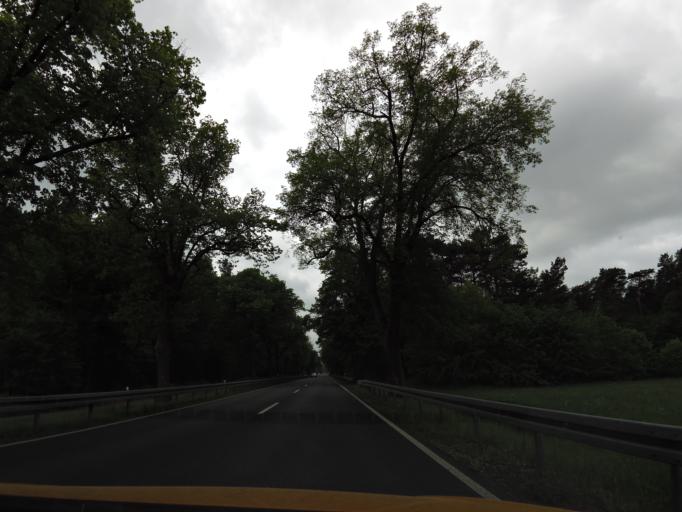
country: DE
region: Brandenburg
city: Beelitz
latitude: 52.1925
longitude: 12.9511
